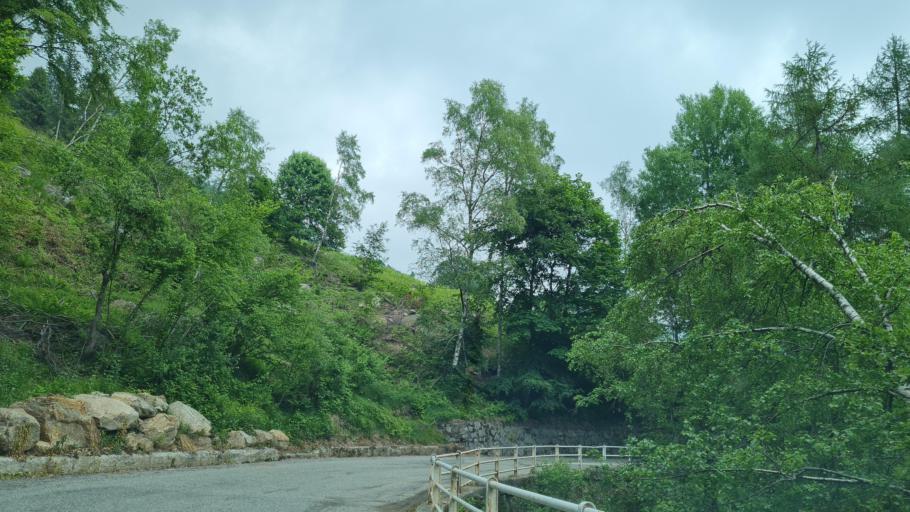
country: IT
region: Piedmont
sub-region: Provincia di Biella
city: Sordevolo
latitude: 45.6090
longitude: 7.9801
